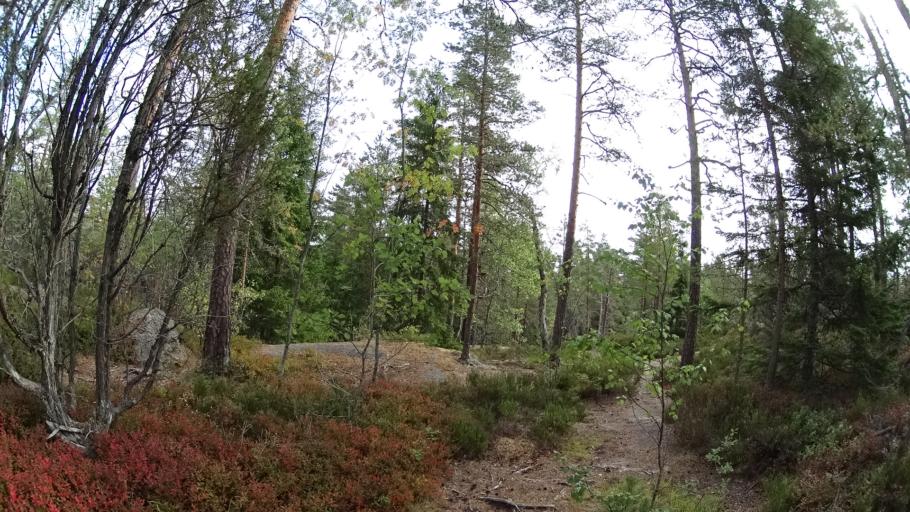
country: FI
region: Uusimaa
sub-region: Helsinki
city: Espoo
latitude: 60.2978
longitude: 24.5838
